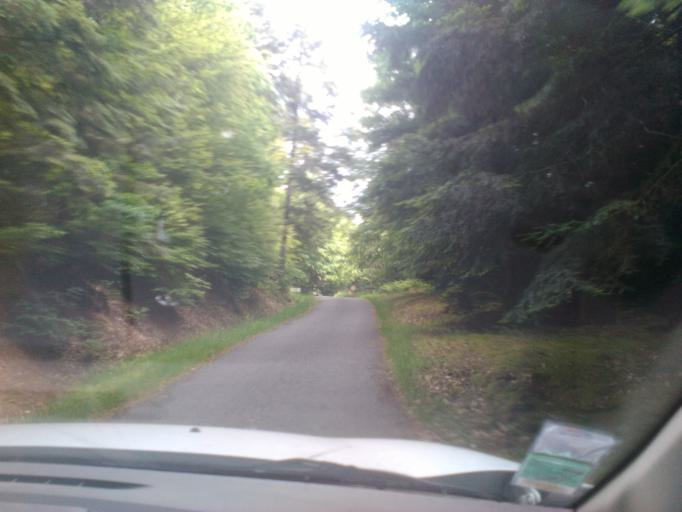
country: FR
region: Lorraine
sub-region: Departement des Vosges
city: Moyenmoutier
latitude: 48.3889
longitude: 6.9352
